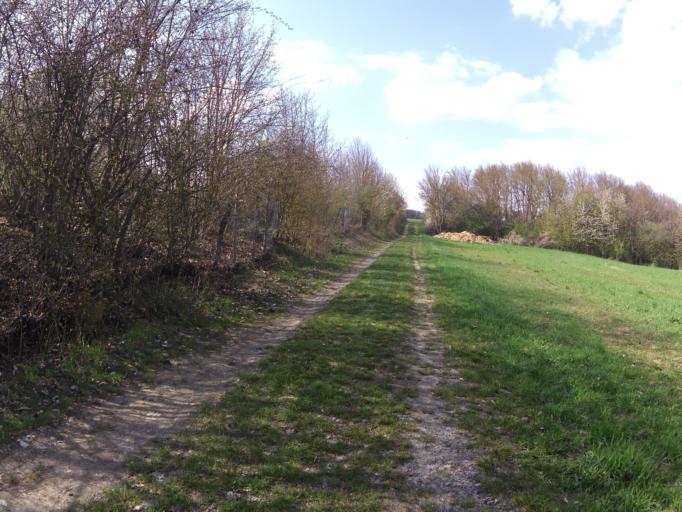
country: DE
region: Bavaria
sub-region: Regierungsbezirk Unterfranken
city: Rimpar
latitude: 49.8683
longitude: 9.9635
